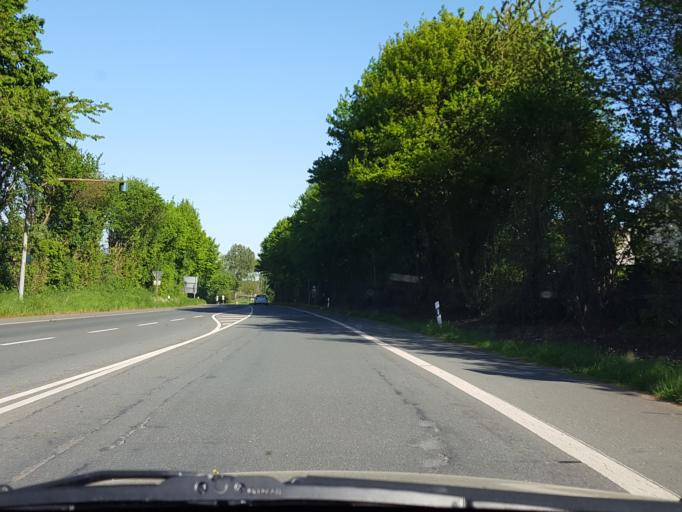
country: DE
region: North Rhine-Westphalia
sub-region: Regierungsbezirk Munster
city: Haltern
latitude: 51.7797
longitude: 7.2097
